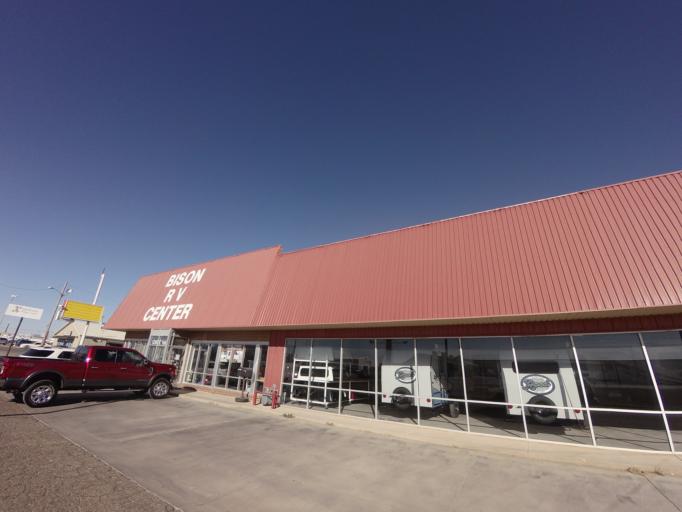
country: US
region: New Mexico
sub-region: Curry County
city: Clovis
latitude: 34.3987
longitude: -103.1911
